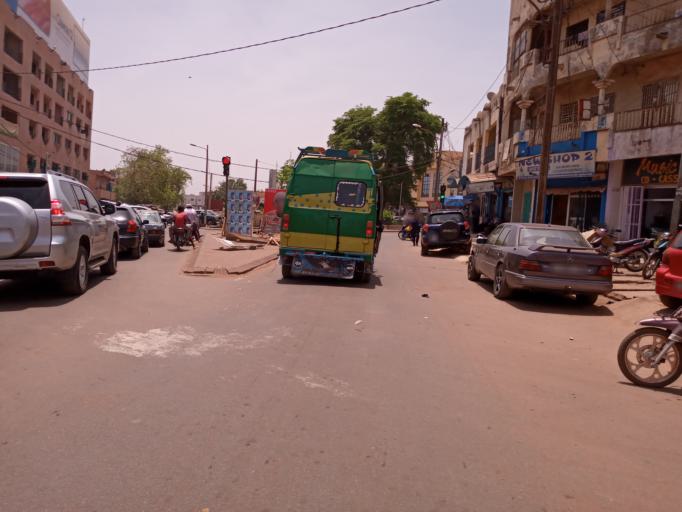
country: ML
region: Bamako
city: Bamako
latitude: 12.6395
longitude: -8.0026
